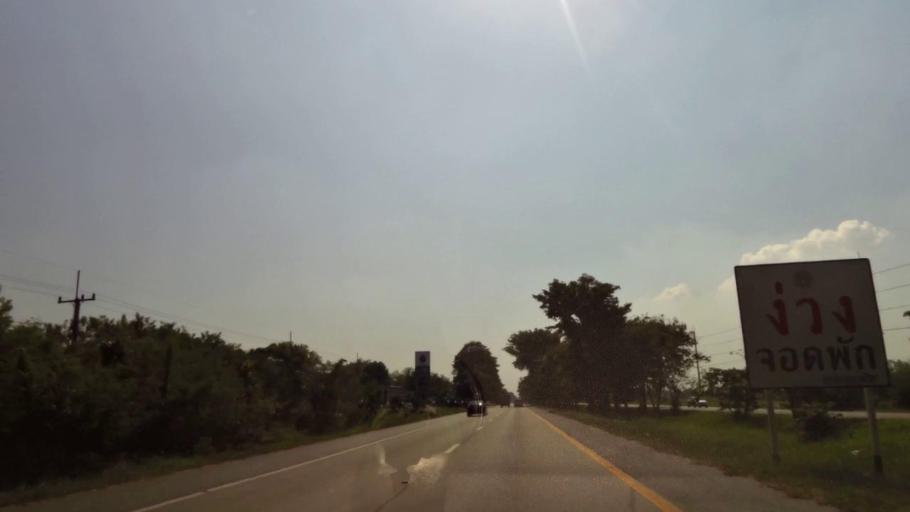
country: TH
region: Phichit
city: Wachira Barami
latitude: 16.5813
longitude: 100.1476
